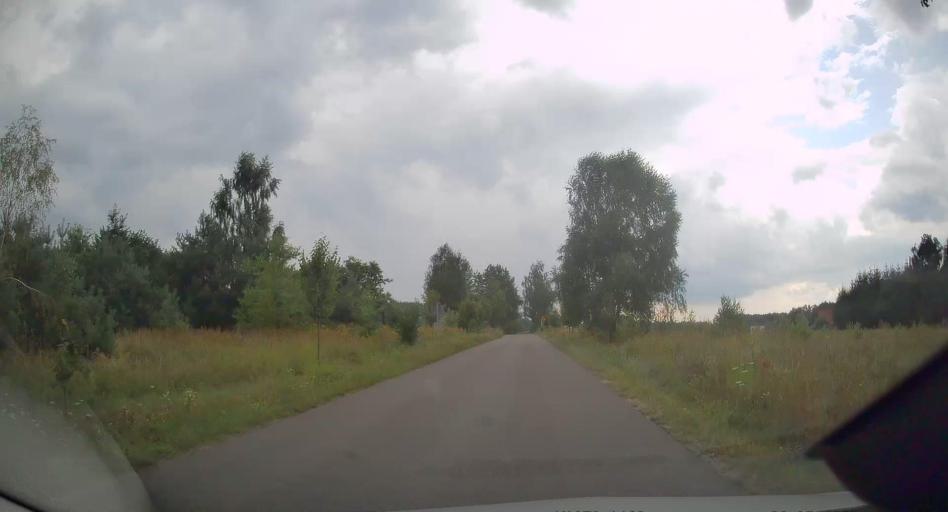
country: PL
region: Lodz Voivodeship
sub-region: Powiat rawski
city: Rawa Mazowiecka
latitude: 51.7485
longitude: 20.2126
